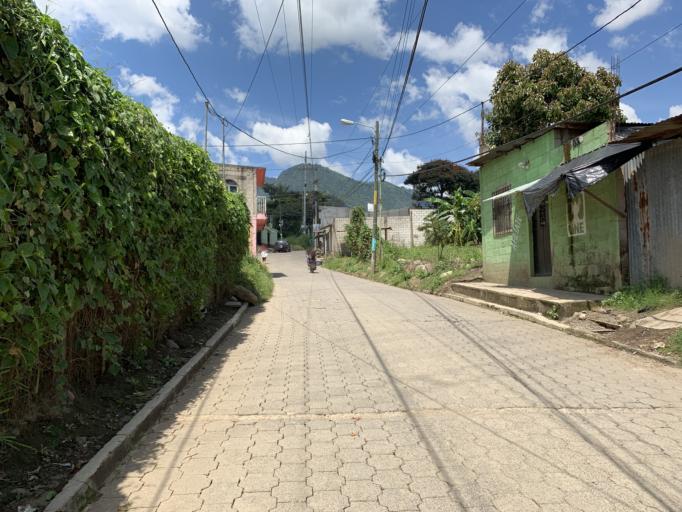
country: GT
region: Guatemala
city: Amatitlan
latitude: 14.4883
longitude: -90.6422
